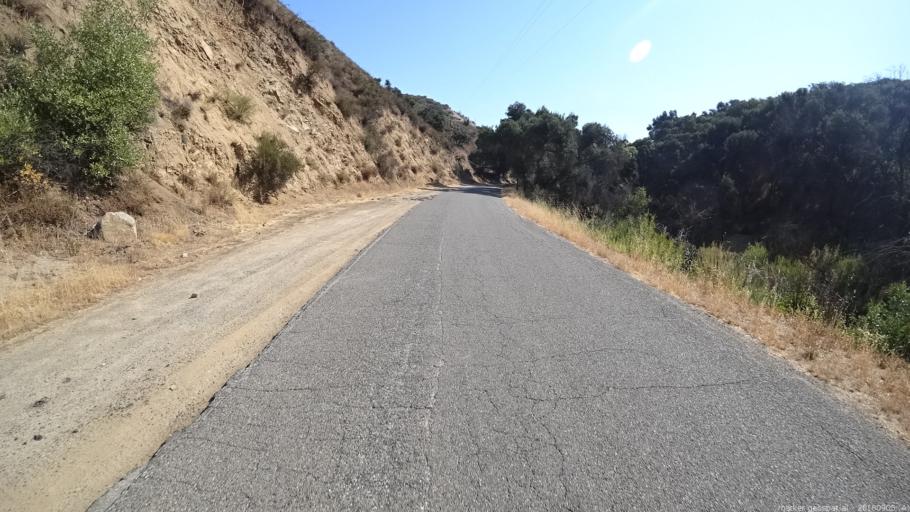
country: US
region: California
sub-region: Monterey County
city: Gonzales
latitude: 36.3935
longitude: -121.5871
